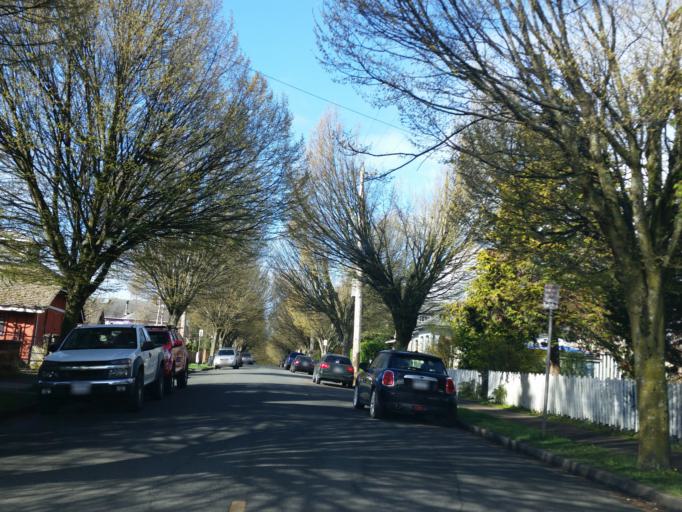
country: CA
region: British Columbia
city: Victoria
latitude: 48.4371
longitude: -123.3888
